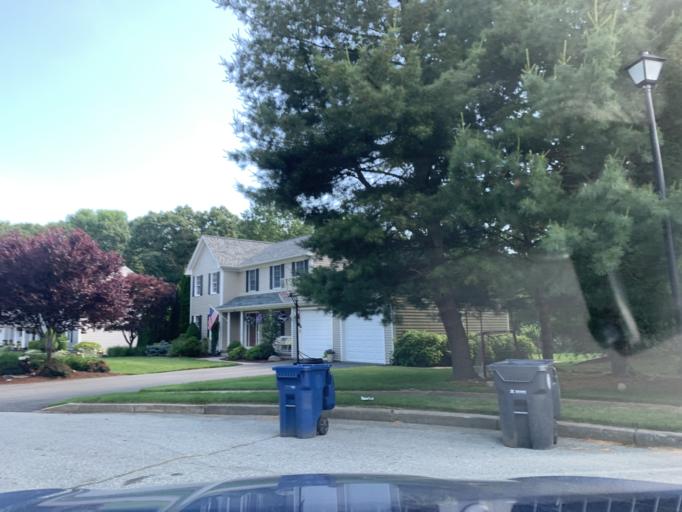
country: US
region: Rhode Island
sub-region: Kent County
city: East Greenwich
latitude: 41.6798
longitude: -71.4667
